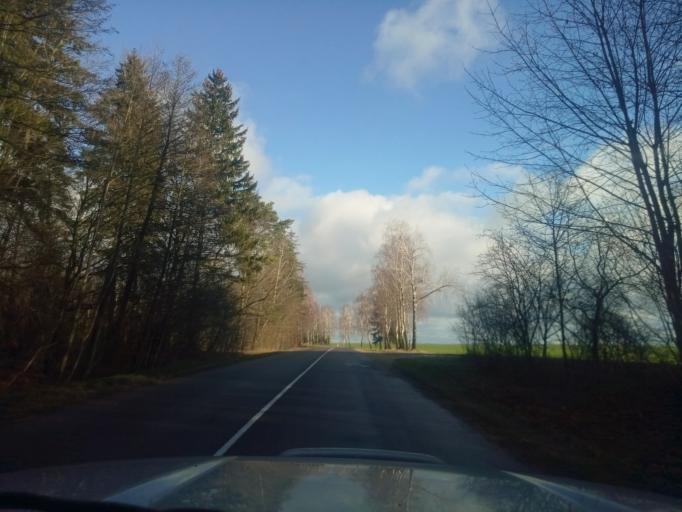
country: BY
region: Minsk
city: Tsimkavichy
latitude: 53.1723
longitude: 26.9341
